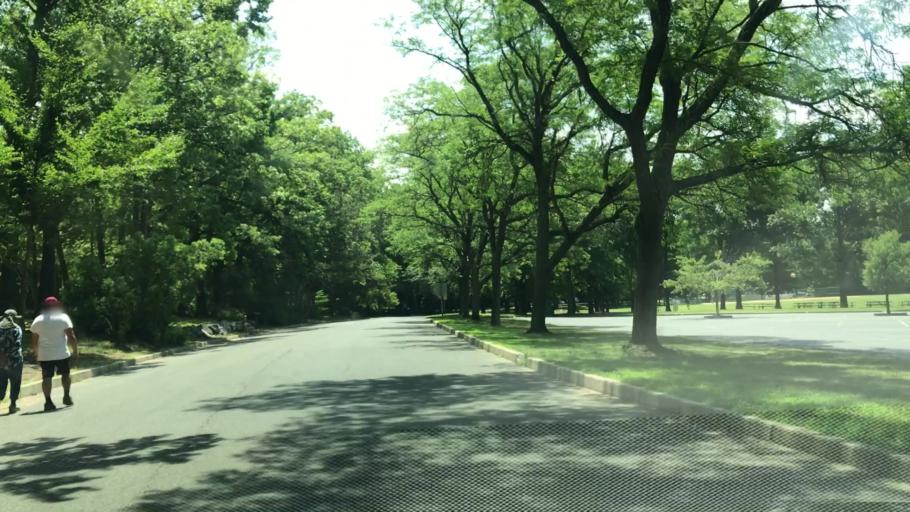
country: US
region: New Jersey
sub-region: Bergen County
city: River Edge
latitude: 40.9297
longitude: -74.0484
